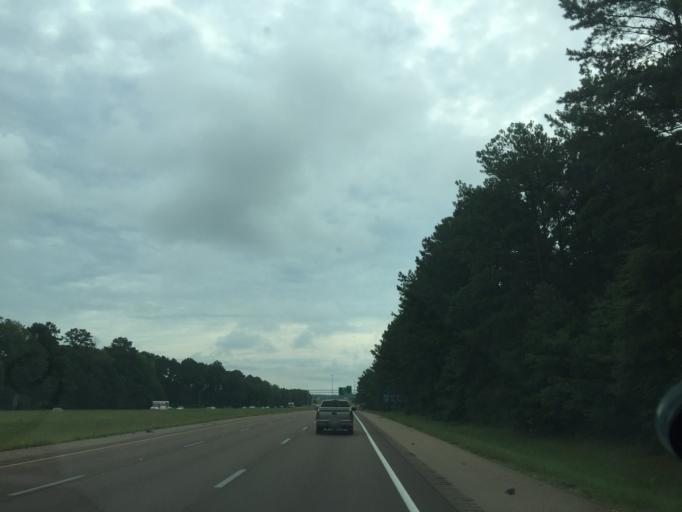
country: US
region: Mississippi
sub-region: Rankin County
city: Brandon
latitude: 32.2746
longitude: -90.0504
